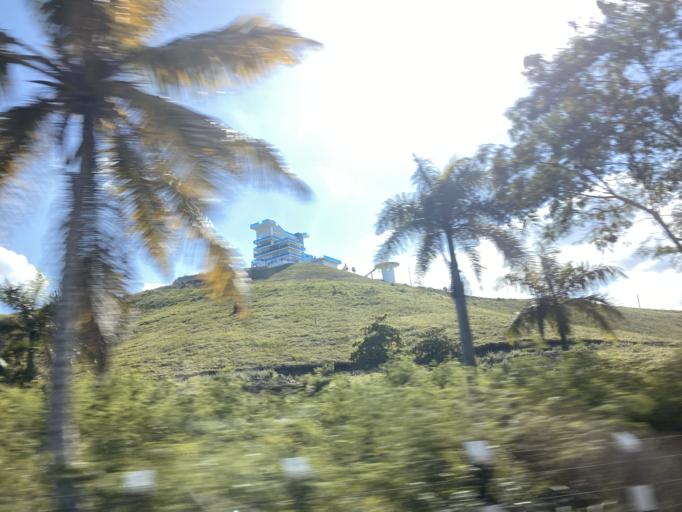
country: DO
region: Espaillat
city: Gaspar Hernandez
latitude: 19.6406
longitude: -70.2565
